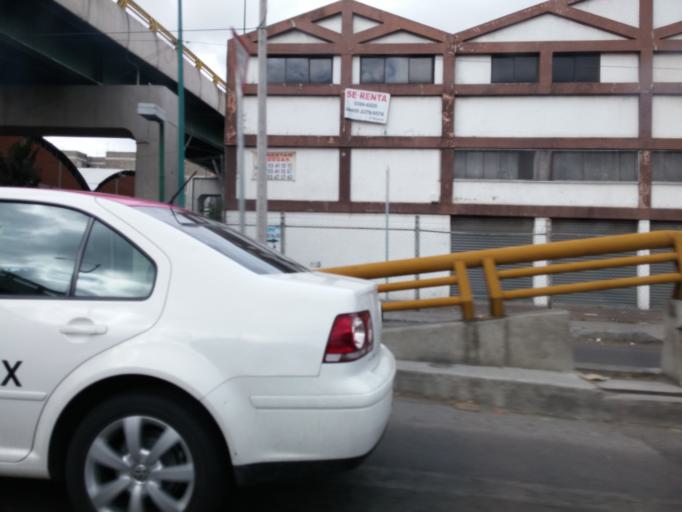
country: MX
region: Mexico City
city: Cuauhtemoc
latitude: 19.4586
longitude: -99.1557
